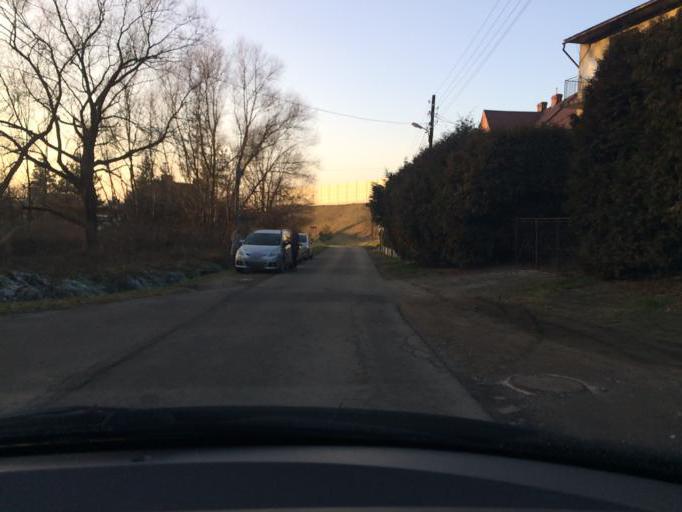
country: PL
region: Lesser Poland Voivodeship
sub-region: Powiat wielicki
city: Czarnochowice
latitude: 50.0053
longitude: 20.0367
